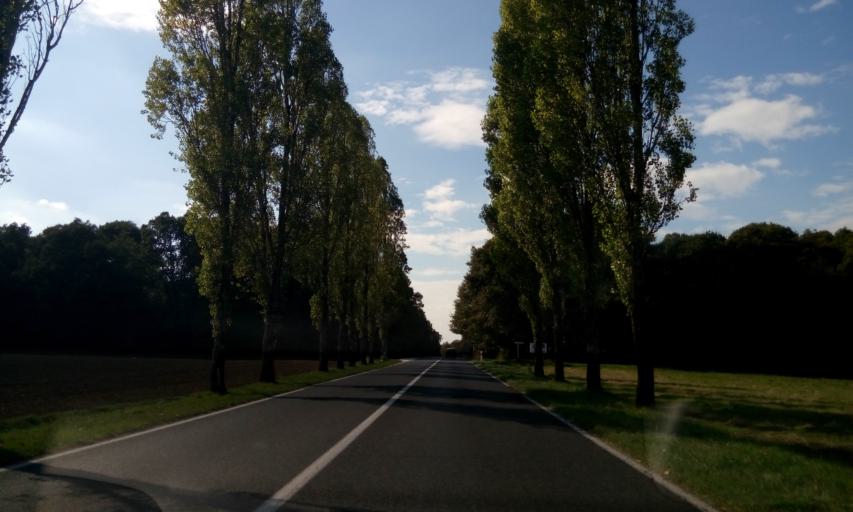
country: FR
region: Centre
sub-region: Departement d'Indre-et-Loire
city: Amboise
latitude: 47.3944
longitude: 0.9927
